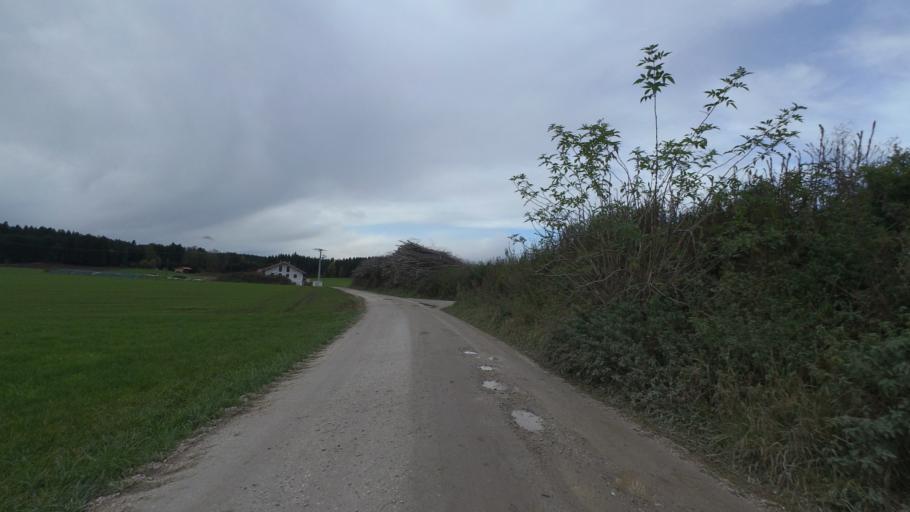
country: DE
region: Bavaria
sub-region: Upper Bavaria
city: Nussdorf
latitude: 47.9108
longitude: 12.5869
